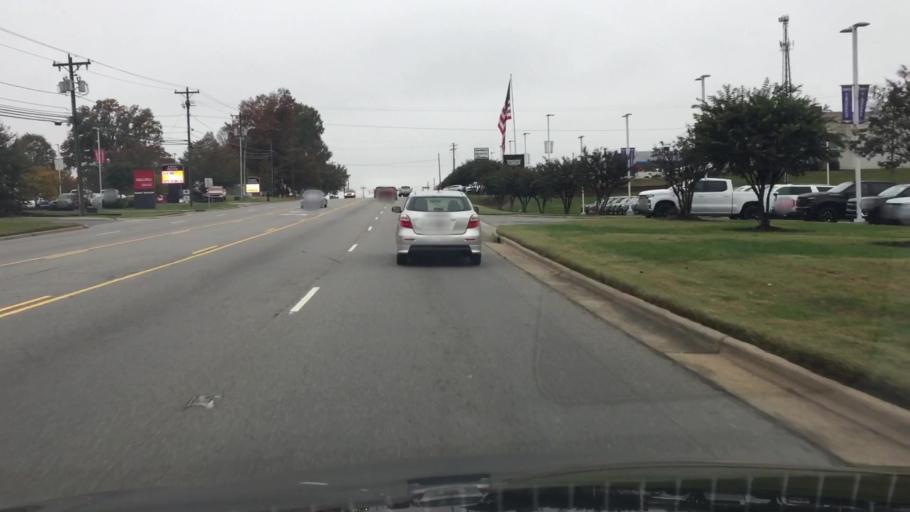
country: US
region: North Carolina
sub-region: Iredell County
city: Mooresville
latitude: 35.5905
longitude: -80.8443
